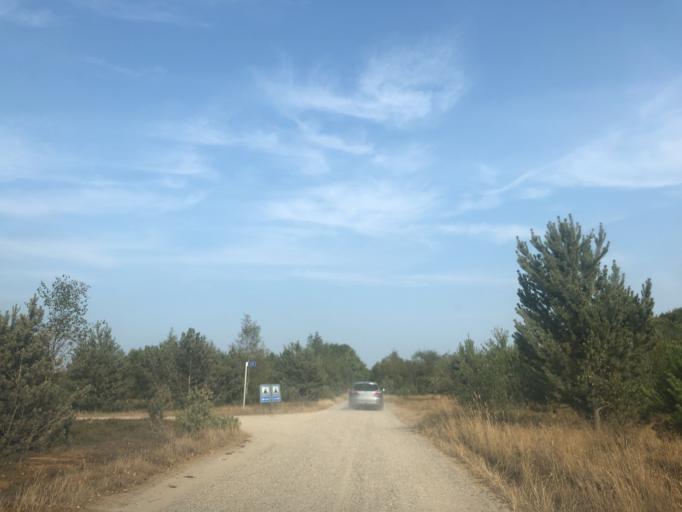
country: DK
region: North Denmark
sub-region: Morso Kommune
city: Nykobing Mors
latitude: 56.8417
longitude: 9.0464
